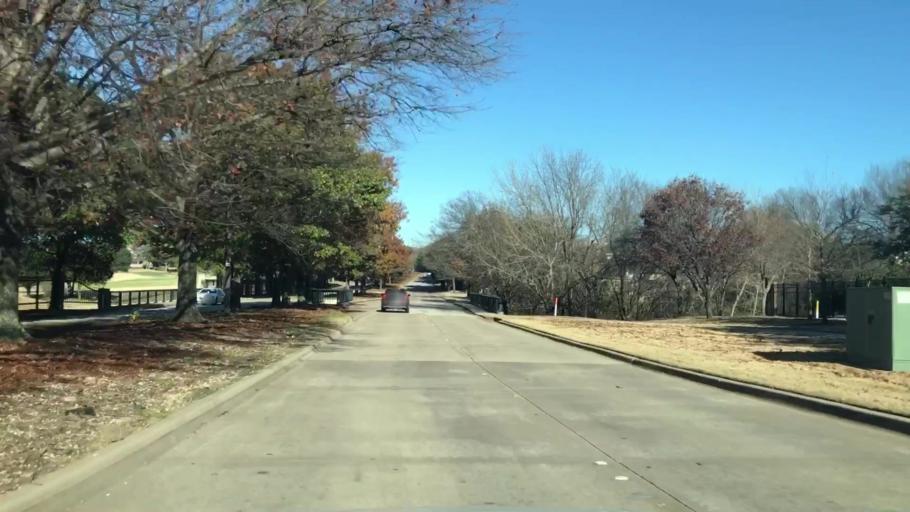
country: US
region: Texas
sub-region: Denton County
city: The Colony
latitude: 33.0941
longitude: -96.8403
